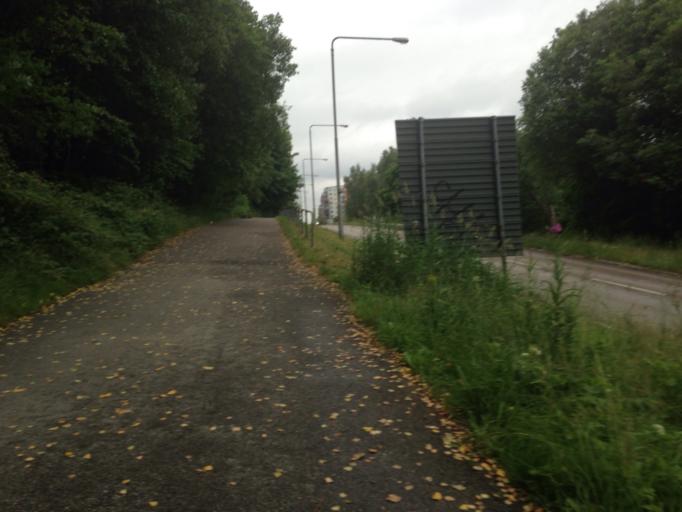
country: SE
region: Vaestra Goetaland
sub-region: Partille Kommun
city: Partille
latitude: 57.7192
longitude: 12.0622
